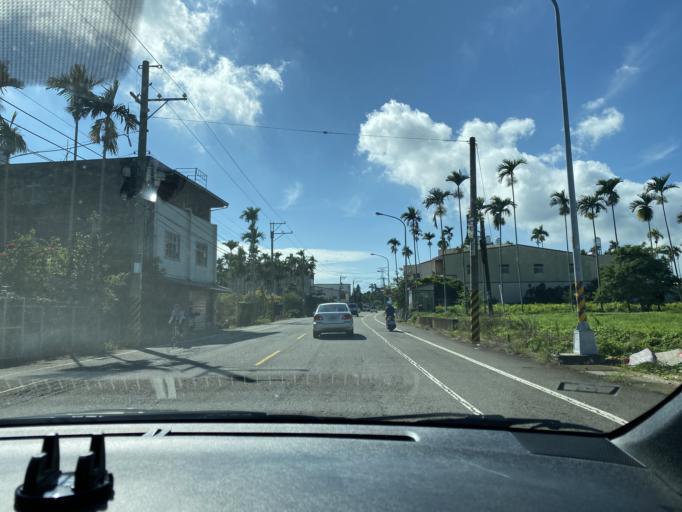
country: TW
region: Taiwan
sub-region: Nantou
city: Nantou
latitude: 23.9546
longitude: 120.6336
